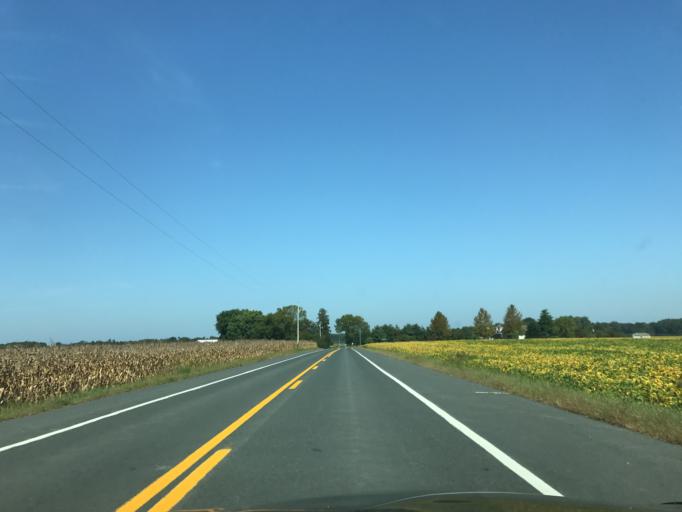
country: US
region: Maryland
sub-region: Queen Anne's County
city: Kingstown
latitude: 39.3311
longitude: -75.9515
